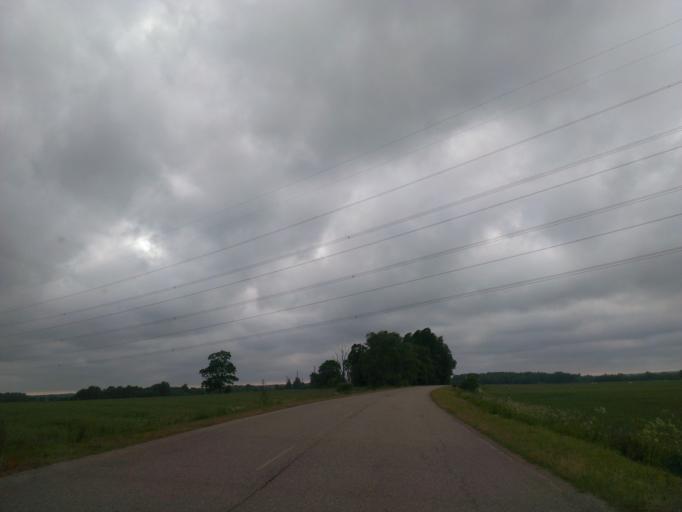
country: LV
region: Aizpute
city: Aizpute
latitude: 56.7228
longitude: 21.4357
